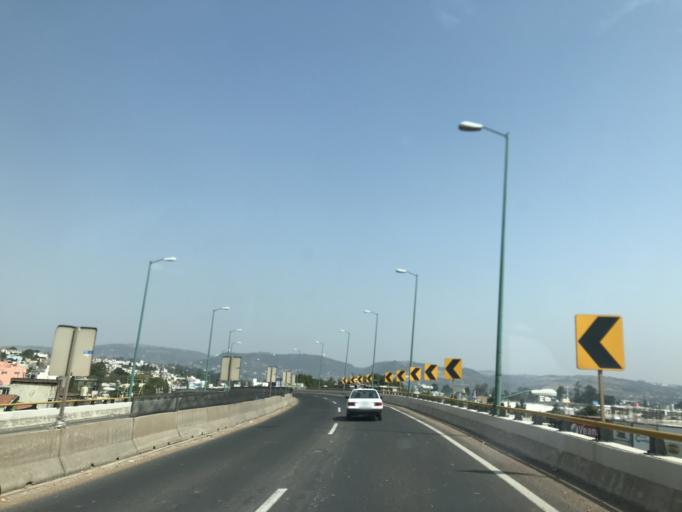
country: MX
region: Tlaxcala
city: Tlaxcala de Xicohtencatl
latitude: 19.3113
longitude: -98.2007
